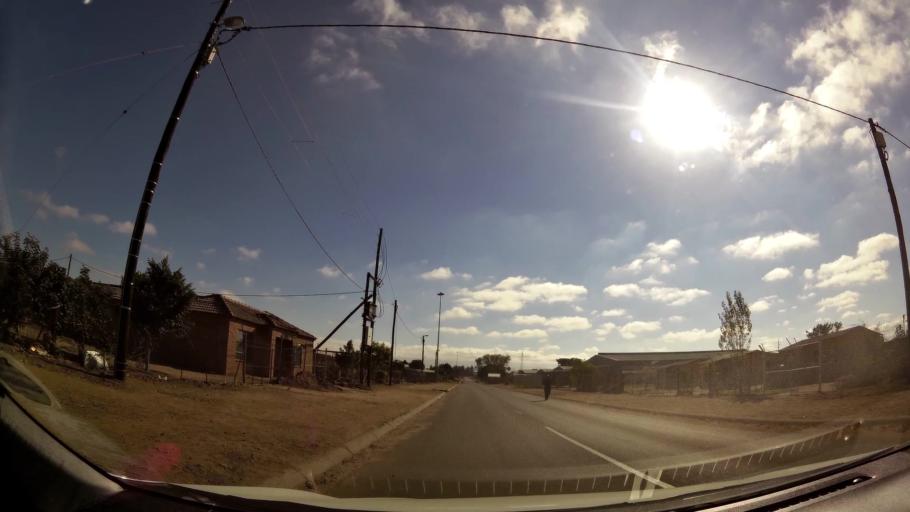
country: ZA
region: Limpopo
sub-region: Capricorn District Municipality
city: Polokwane
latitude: -23.8472
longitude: 29.4000
